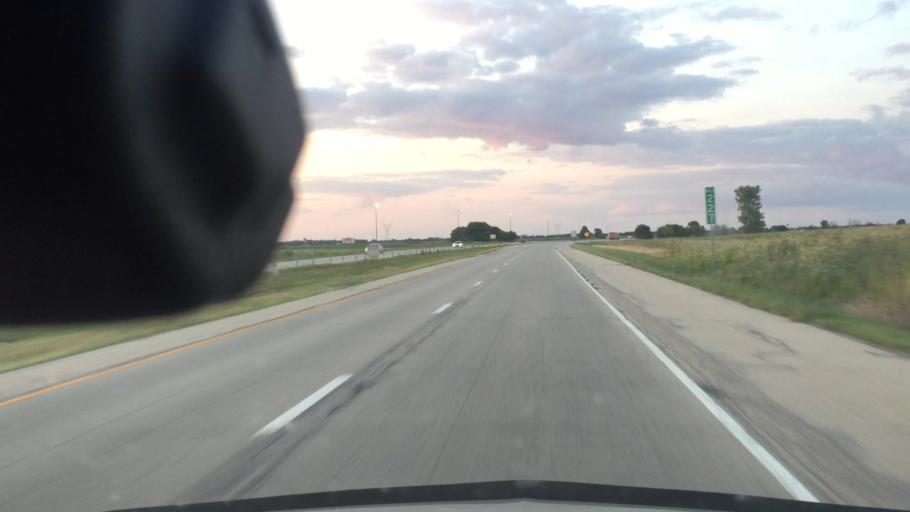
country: US
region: Illinois
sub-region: Grundy County
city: Gardner
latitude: 41.1860
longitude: -88.3216
